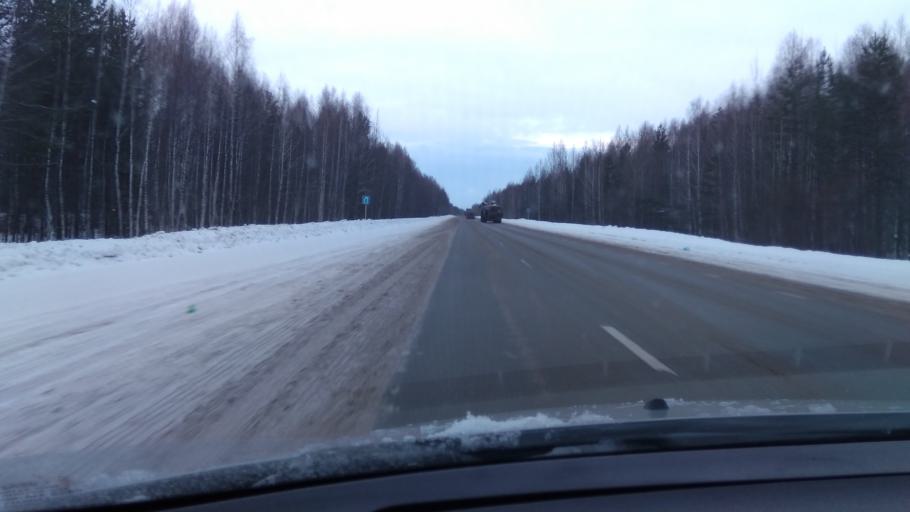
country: RU
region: Sverdlovsk
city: Tsementnyy
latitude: 57.4175
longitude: 60.2108
